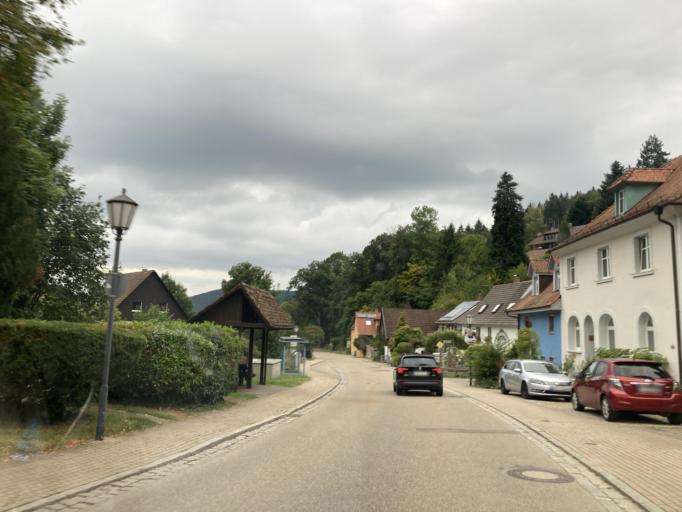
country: DE
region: Baden-Wuerttemberg
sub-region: Freiburg Region
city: Badenweiler
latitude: 47.8069
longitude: 7.7007
